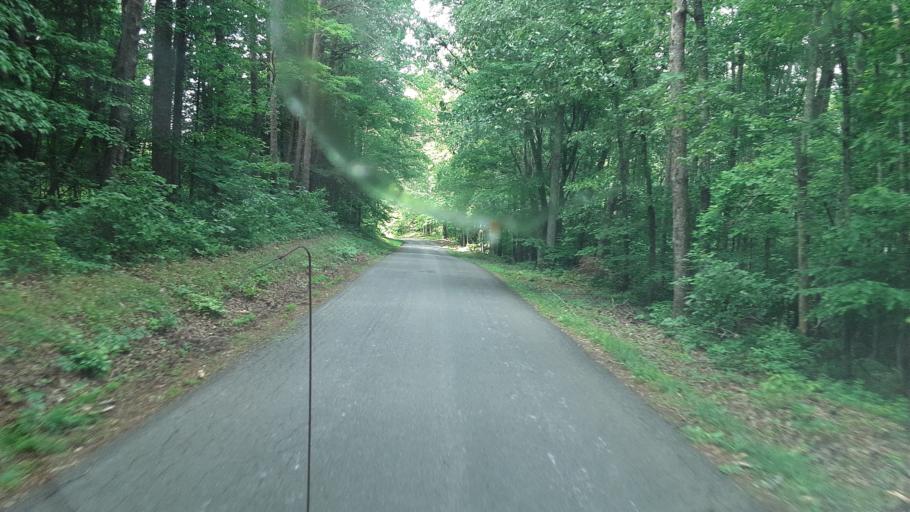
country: US
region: Virginia
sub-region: Pittsylvania County
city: Chatham
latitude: 36.8523
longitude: -79.4514
